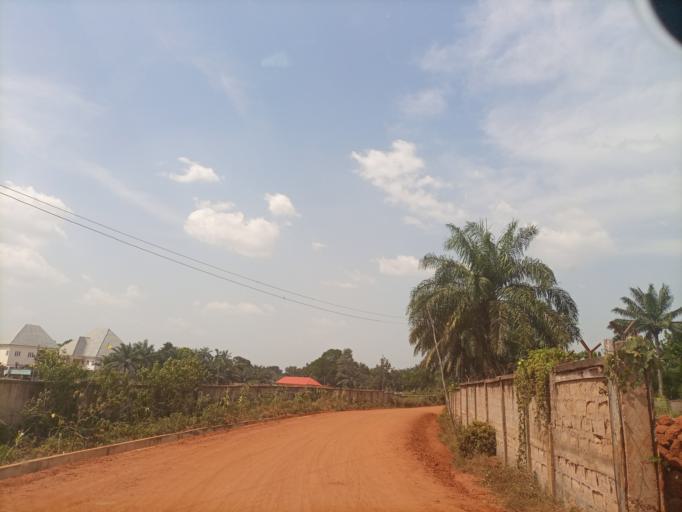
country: NG
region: Enugu
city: Obollo-Afor
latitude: 6.8633
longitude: 7.4742
